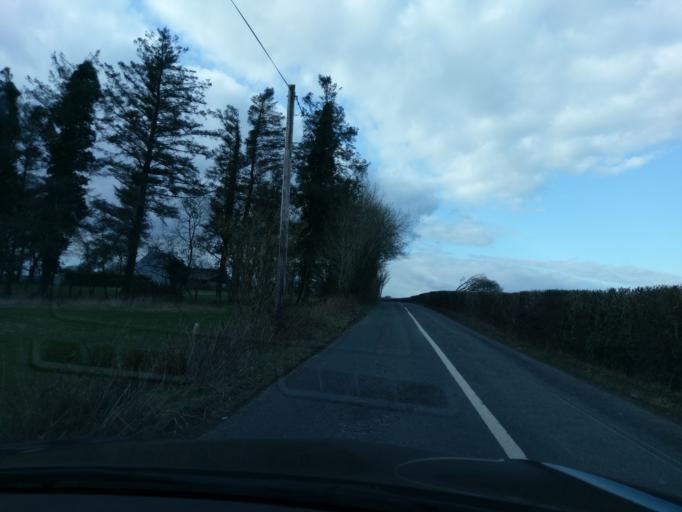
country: IE
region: Connaught
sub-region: County Galway
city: Athenry
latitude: 53.4942
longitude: -8.5977
